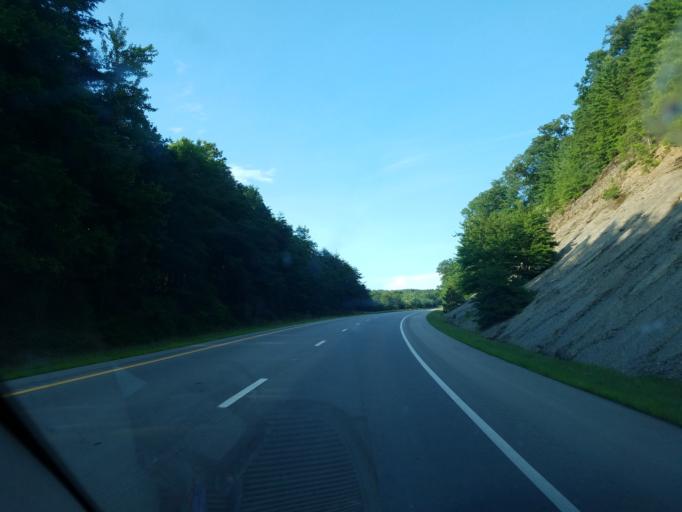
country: US
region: Ohio
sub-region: Adams County
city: Peebles
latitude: 39.0137
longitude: -83.2944
